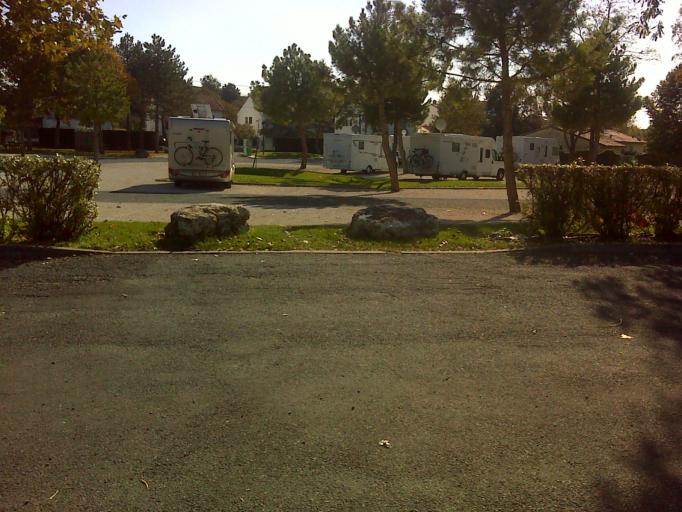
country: FR
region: Poitou-Charentes
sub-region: Departement de la Charente-Maritime
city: Royan
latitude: 45.6288
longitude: -1.0127
